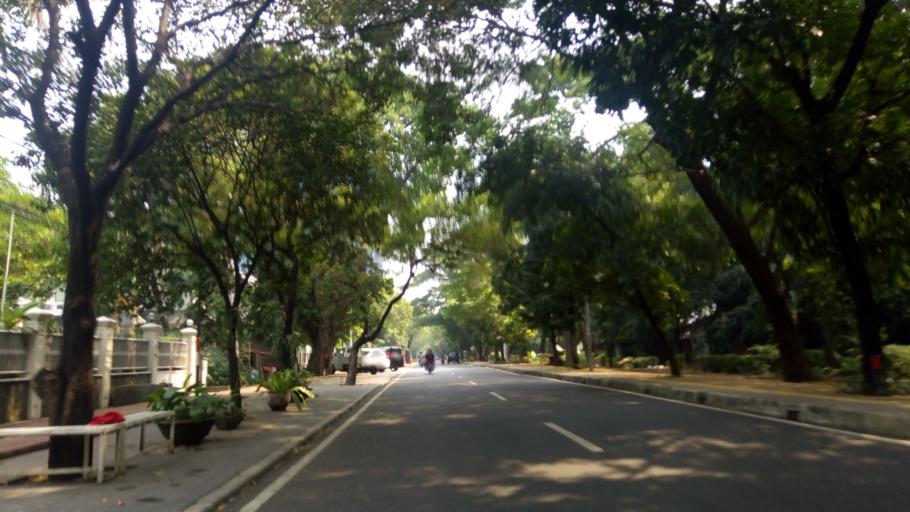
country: ID
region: Jakarta Raya
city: Jakarta
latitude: -6.2017
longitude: 106.8266
